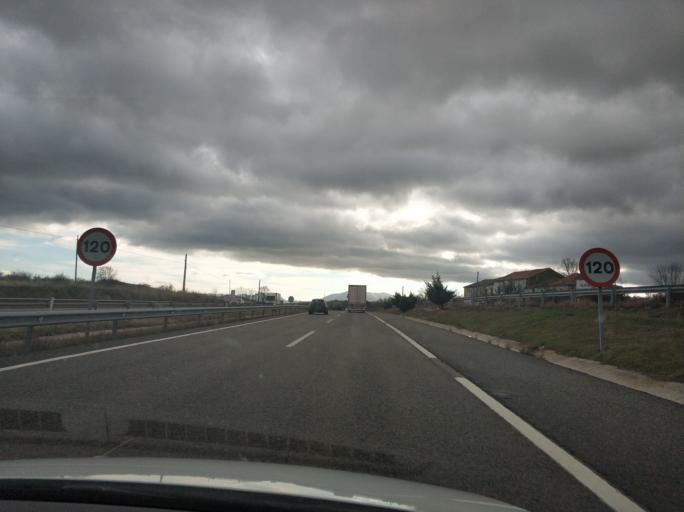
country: ES
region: Madrid
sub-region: Provincia de Madrid
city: Horcajo de la Sierra
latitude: 41.0553
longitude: -3.6140
